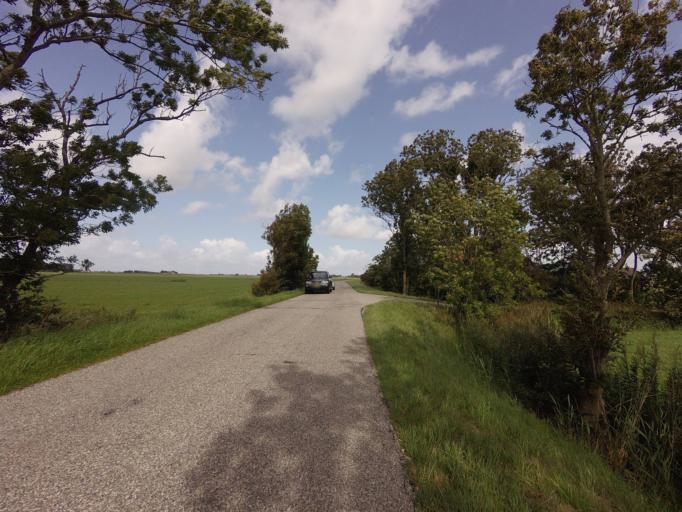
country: NL
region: Friesland
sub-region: Gemeente Franekeradeel
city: Sexbierum
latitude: 53.1605
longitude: 5.4835
